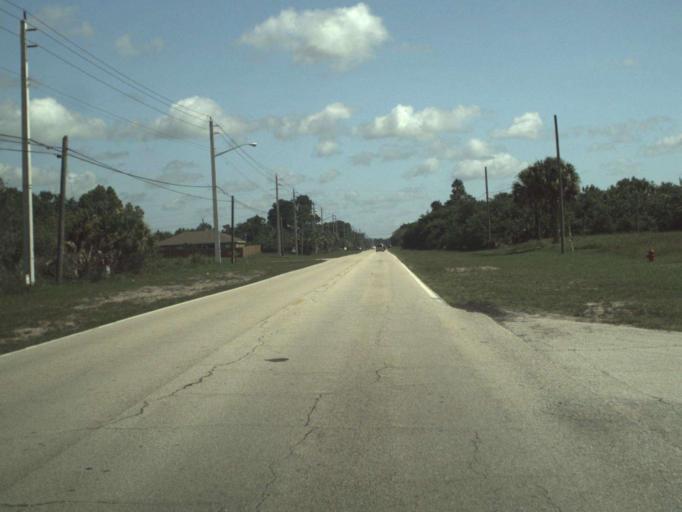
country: US
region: Florida
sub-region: Saint Lucie County
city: Port Saint Lucie
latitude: 27.2357
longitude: -80.3769
